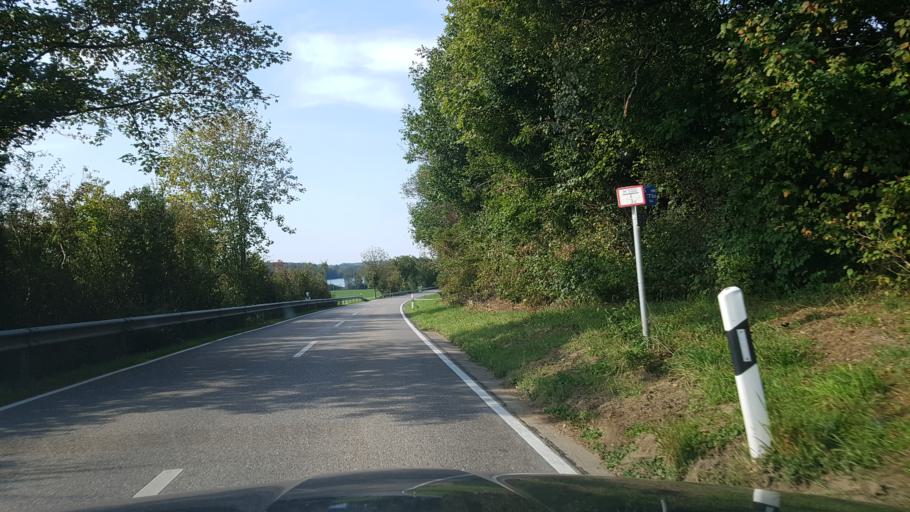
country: DE
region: Bavaria
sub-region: Upper Bavaria
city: Laufen
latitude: 47.8995
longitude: 12.9153
